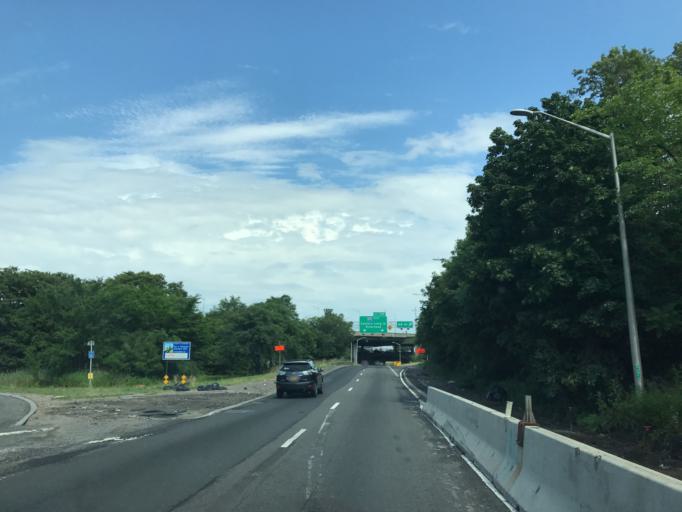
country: US
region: New York
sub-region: Queens County
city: Long Island City
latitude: 40.7328
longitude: -73.9229
